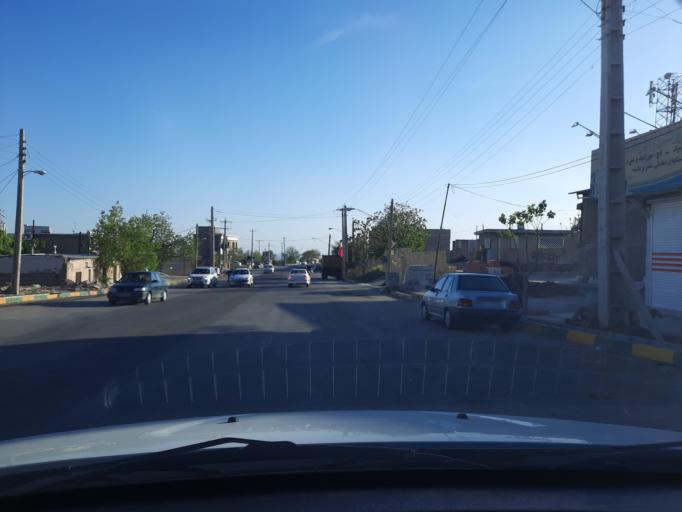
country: IR
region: Qazvin
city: Qazvin
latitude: 36.3320
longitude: 50.1508
